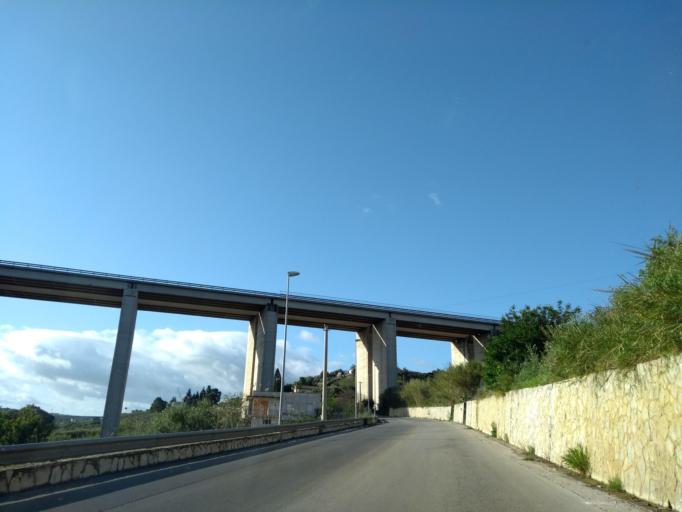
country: IT
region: Sicily
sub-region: Trapani
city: Alcamo
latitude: 38.0154
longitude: 12.9521
